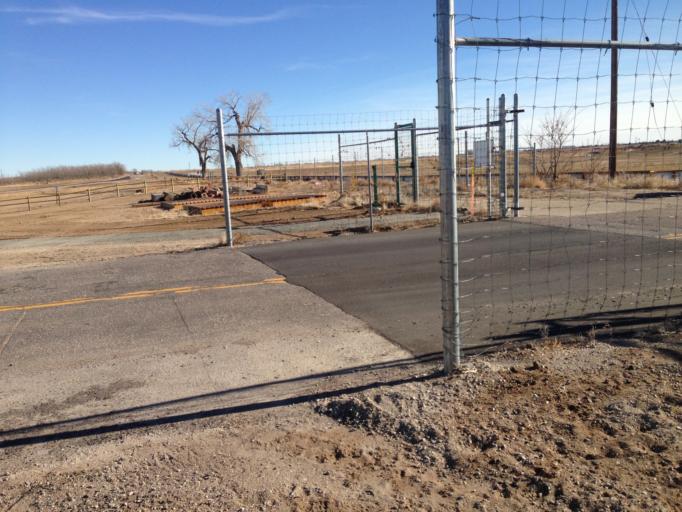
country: US
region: Colorado
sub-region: Adams County
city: Derby
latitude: 39.8130
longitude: -104.8847
